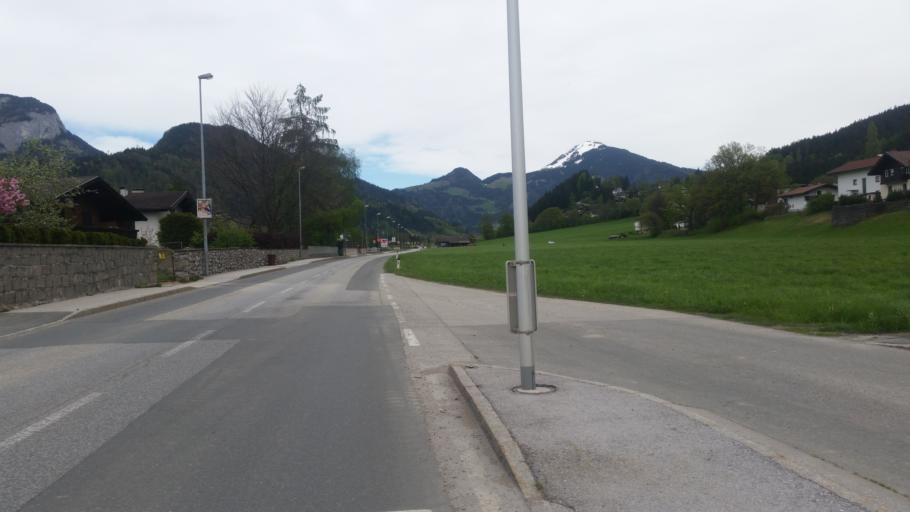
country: AT
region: Tyrol
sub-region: Politischer Bezirk Kufstein
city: Worgl
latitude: 47.4887
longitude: 12.0855
